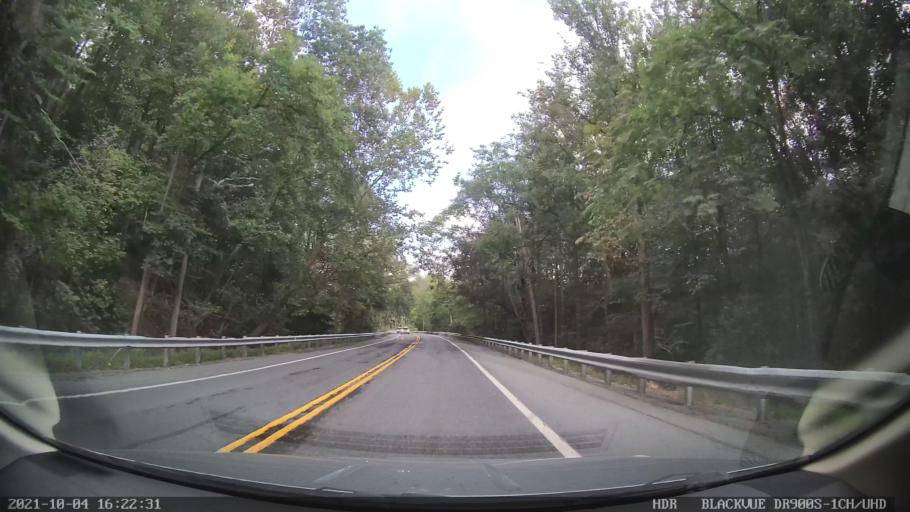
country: US
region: Pennsylvania
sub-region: Berks County
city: Blandon
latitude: 40.4263
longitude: -75.8717
